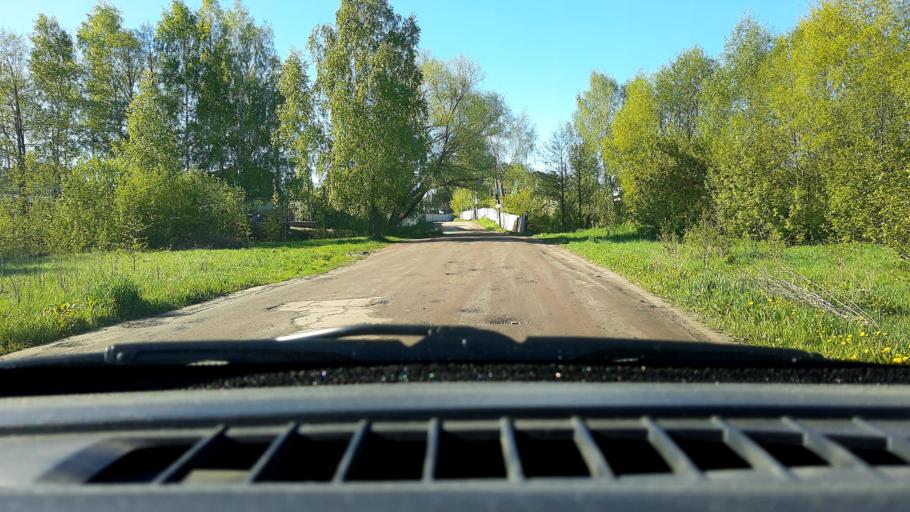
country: RU
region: Nizjnij Novgorod
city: Gorbatovka
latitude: 56.3867
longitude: 43.8057
